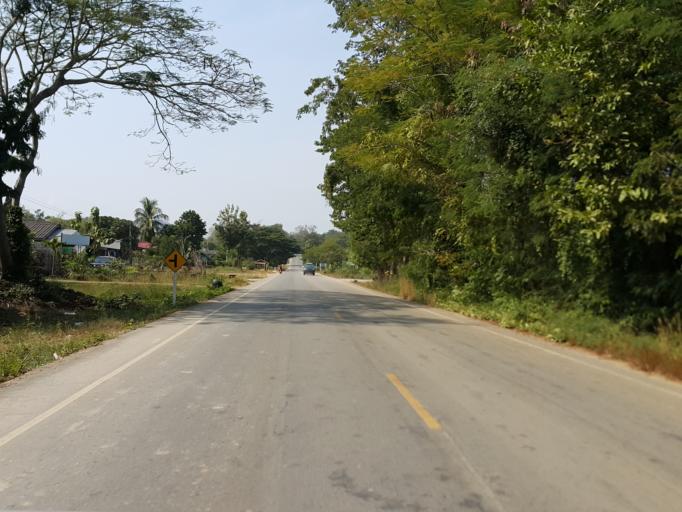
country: TH
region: Sukhothai
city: Thung Saliam
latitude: 17.3353
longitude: 99.4824
